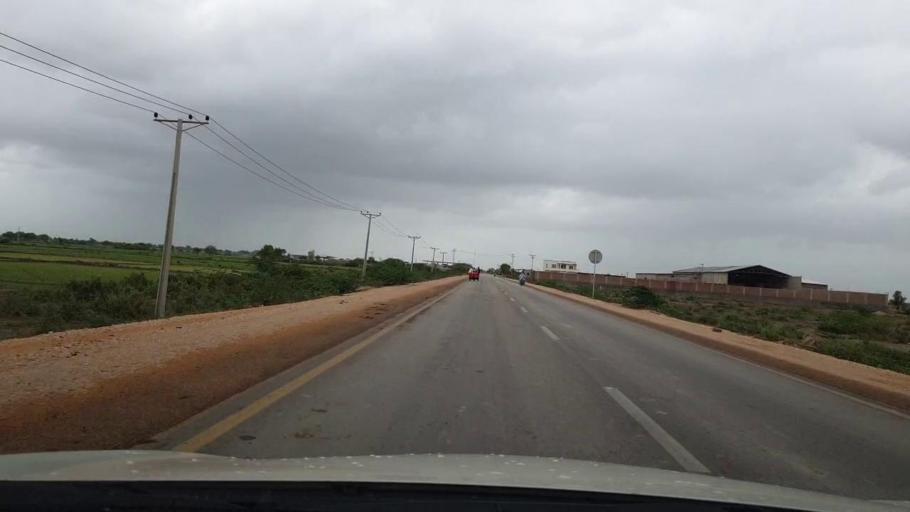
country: PK
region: Sindh
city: Badin
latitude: 24.6528
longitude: 68.7704
